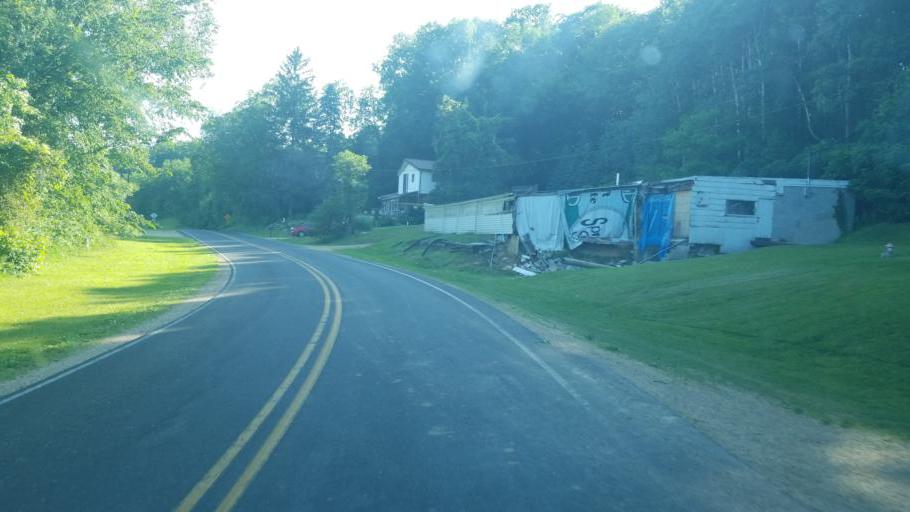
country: US
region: Wisconsin
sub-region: Vernon County
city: Hillsboro
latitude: 43.6779
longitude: -90.3513
